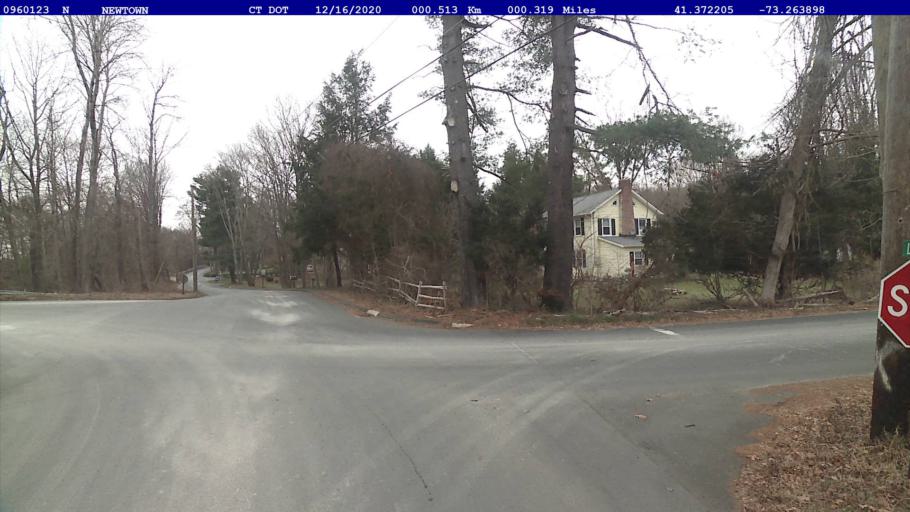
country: US
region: Connecticut
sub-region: Fairfield County
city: Newtown
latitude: 41.3722
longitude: -73.2639
